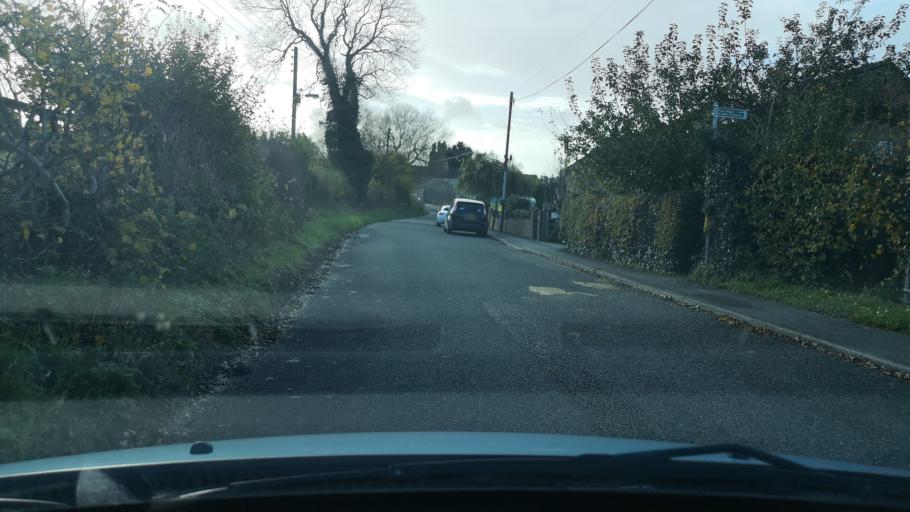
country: GB
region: England
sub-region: City and Borough of Wakefield
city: Ryhill
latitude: 53.6372
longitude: -1.4213
